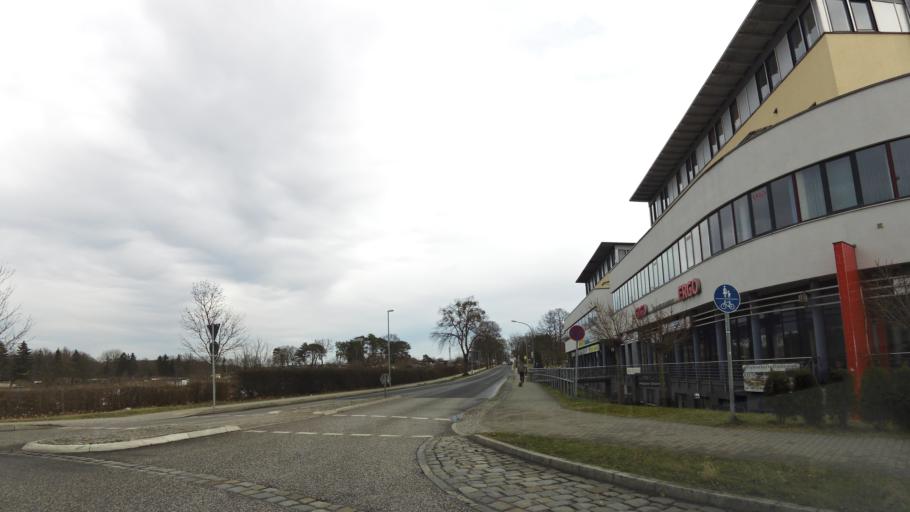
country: DE
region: Brandenburg
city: Strausberg
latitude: 52.5878
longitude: 13.8947
